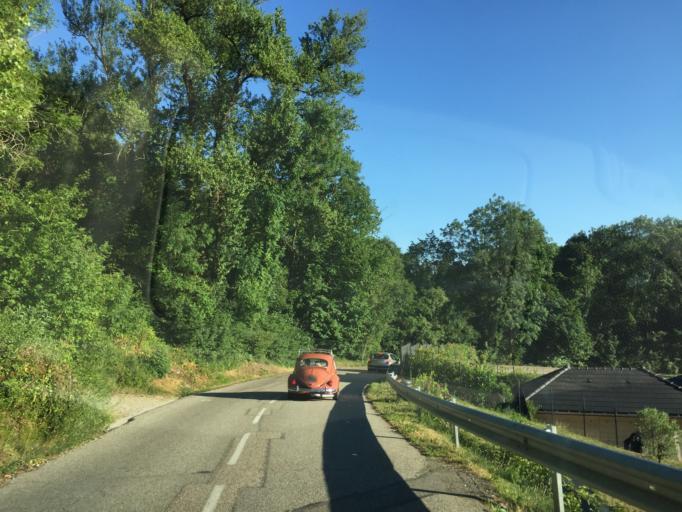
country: FR
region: Rhone-Alpes
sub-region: Departement de la Savoie
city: Challes-les-Eaux
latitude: 45.5408
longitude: 6.0073
